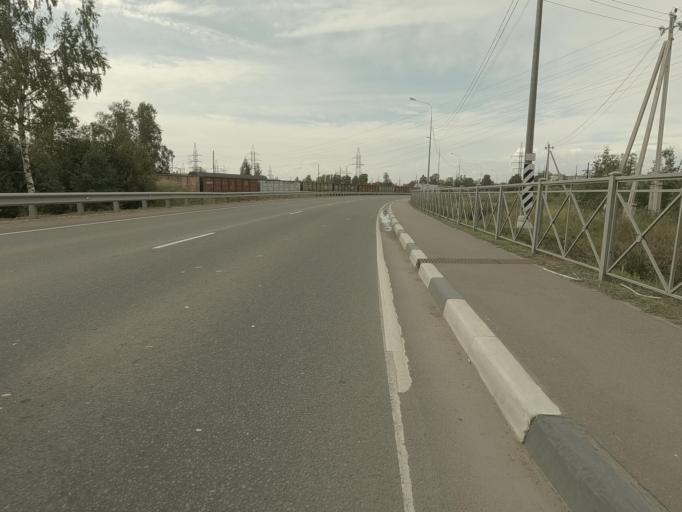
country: RU
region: Leningrad
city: Kirovsk
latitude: 59.8663
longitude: 30.9906
